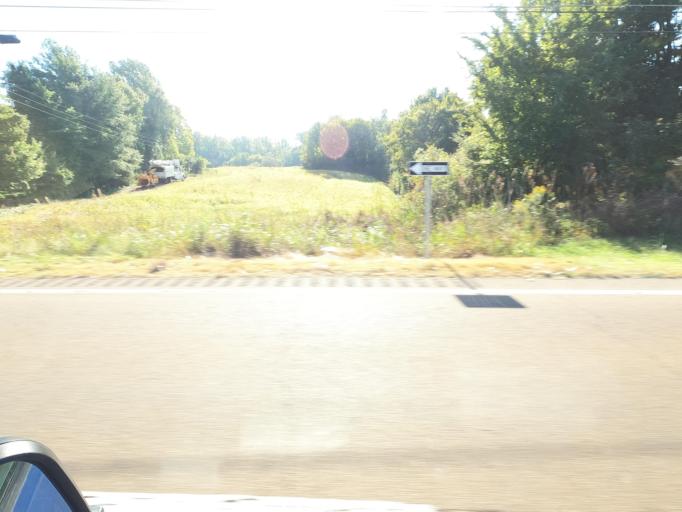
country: US
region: Tennessee
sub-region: Tipton County
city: Munford
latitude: 35.4062
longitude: -89.8385
